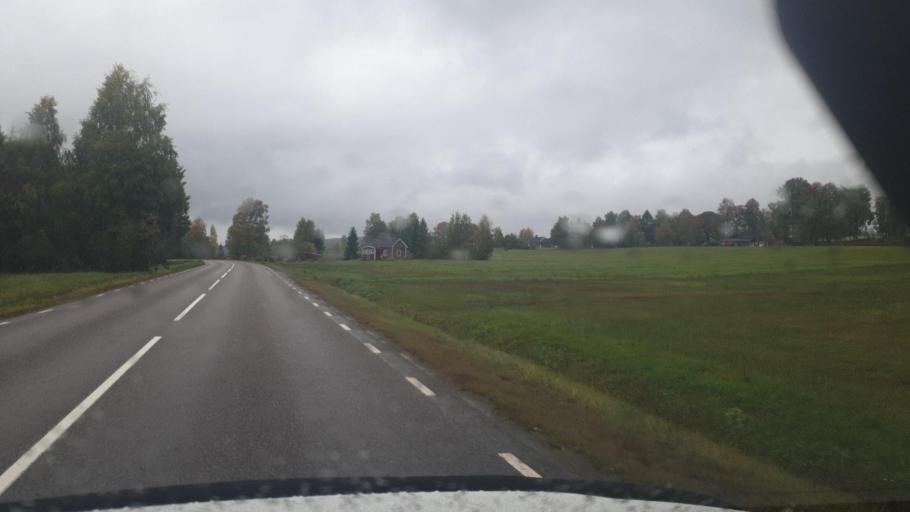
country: SE
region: Vaermland
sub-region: Sunne Kommun
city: Sunne
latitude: 59.7952
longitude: 13.0698
